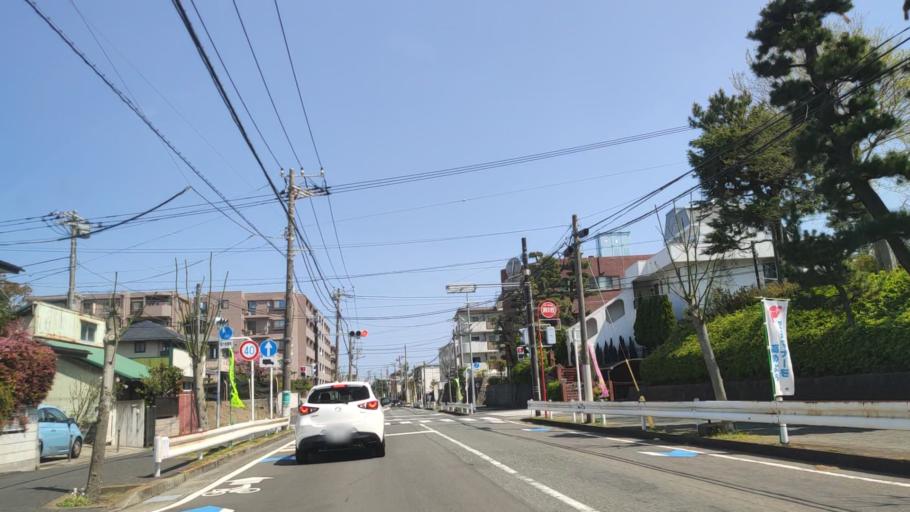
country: JP
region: Kanagawa
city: Hiratsuka
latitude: 35.3196
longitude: 139.3453
